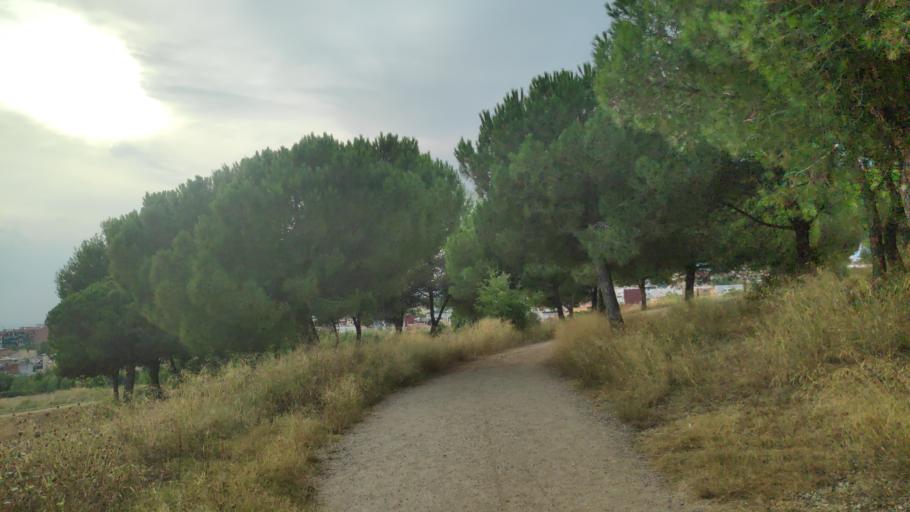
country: ES
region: Catalonia
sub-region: Provincia de Barcelona
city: Rubi
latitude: 41.4969
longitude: 2.0476
